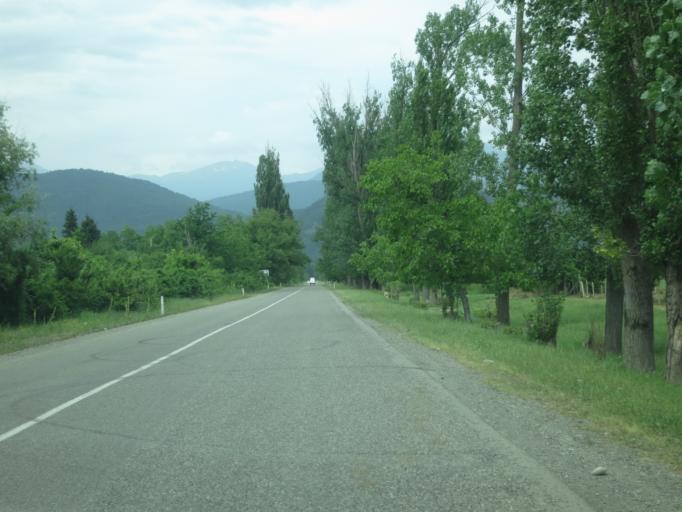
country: GE
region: Kakheti
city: Tsinandali
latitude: 41.9913
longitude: 45.5853
